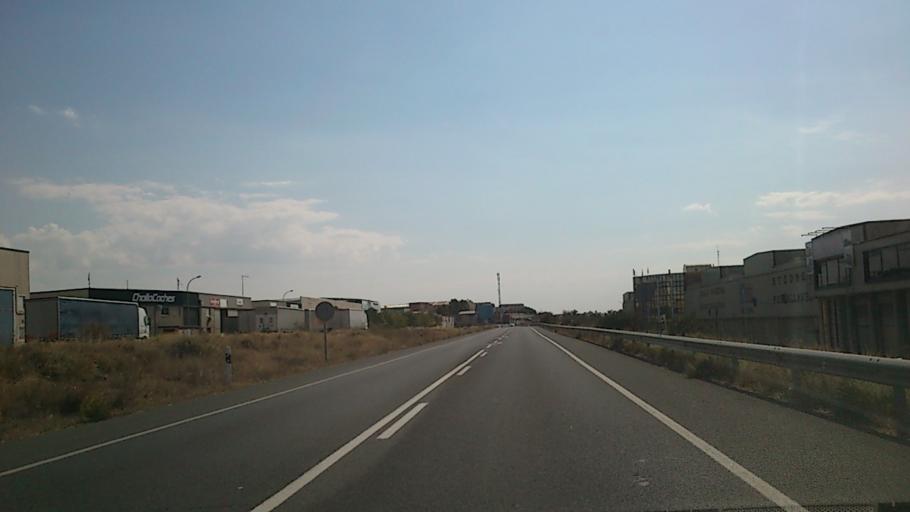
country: ES
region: Aragon
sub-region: Provincia de Zaragoza
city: Puebla de Alfinden
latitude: 41.6414
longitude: -0.7698
